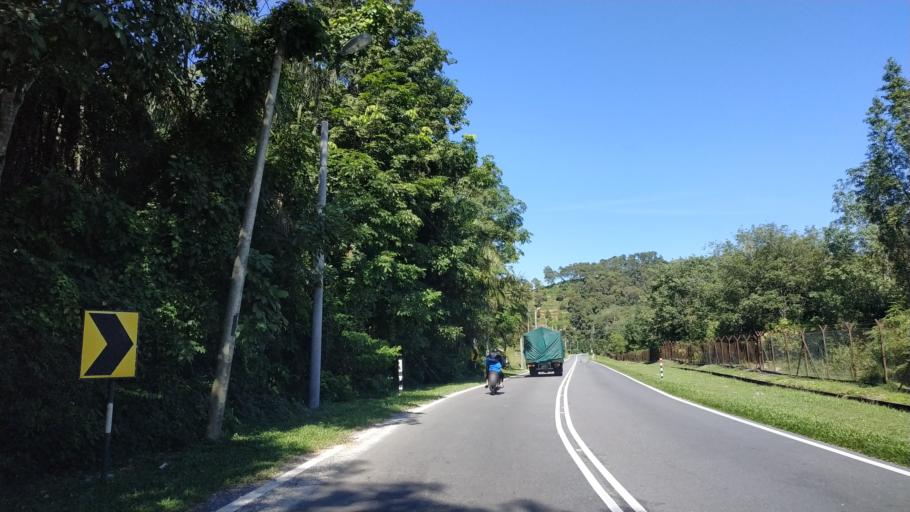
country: MY
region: Kedah
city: Kulim
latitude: 5.3241
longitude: 100.5346
